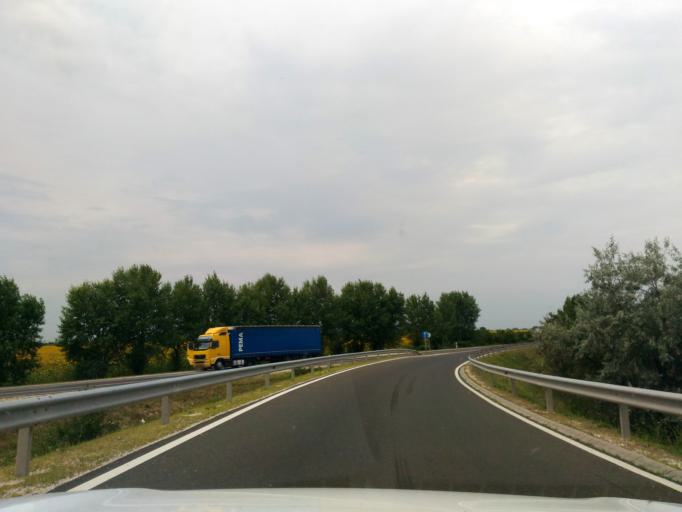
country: HU
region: Jasz-Nagykun-Szolnok
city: Zagyvarekas
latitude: 47.1834
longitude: 20.0984
